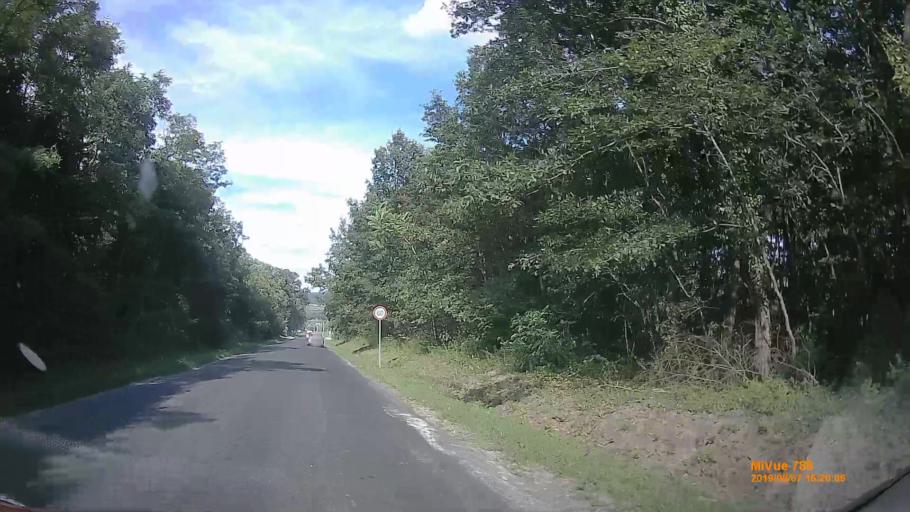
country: HU
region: Zala
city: Cserszegtomaj
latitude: 46.8588
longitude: 17.2711
